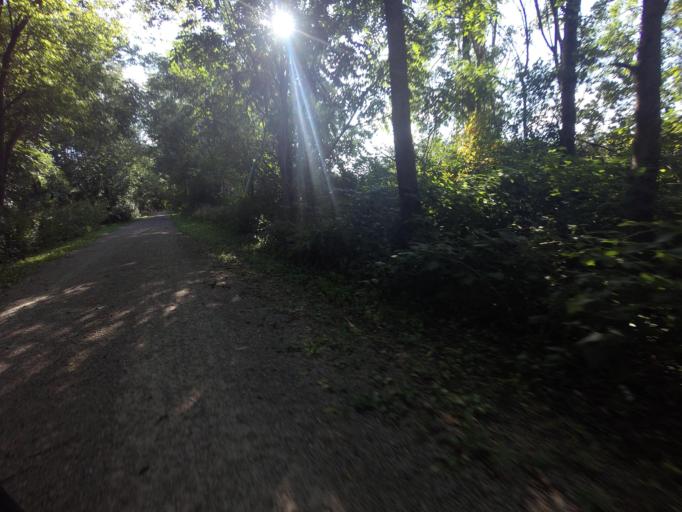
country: CA
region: Ontario
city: Huron East
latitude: 43.7392
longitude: -81.4322
